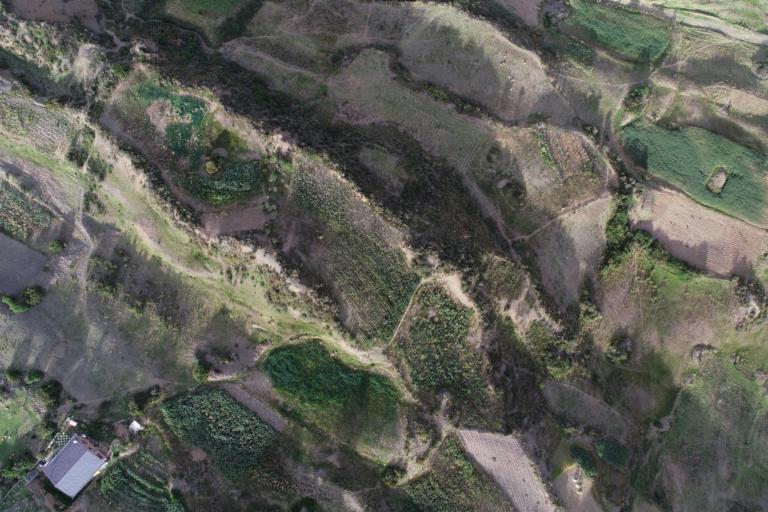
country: BO
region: La Paz
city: La Paz
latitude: -16.5479
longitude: -67.9983
